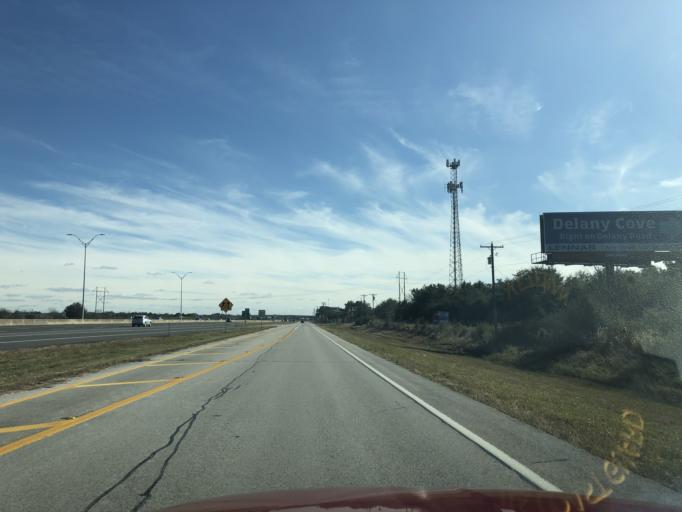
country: US
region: Texas
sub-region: Galveston County
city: Hitchcock
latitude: 29.3946
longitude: -95.0255
